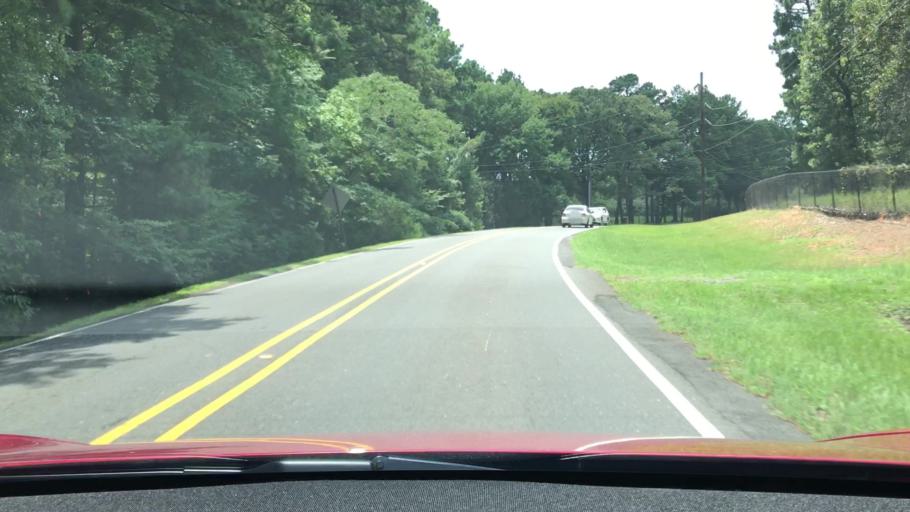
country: US
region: Louisiana
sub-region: De Soto Parish
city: Stonewall
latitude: 32.3668
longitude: -93.6973
